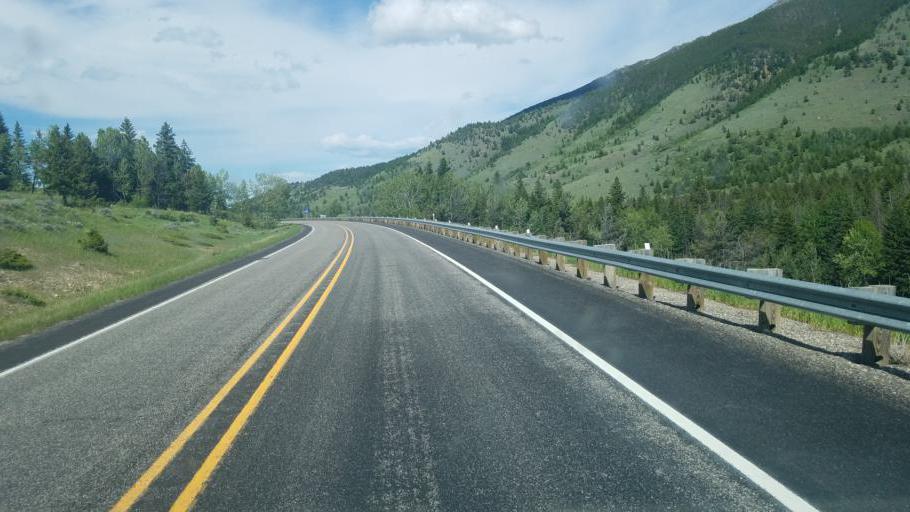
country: US
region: Montana
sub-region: Carbon County
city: Red Lodge
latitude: 45.1015
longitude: -109.3103
